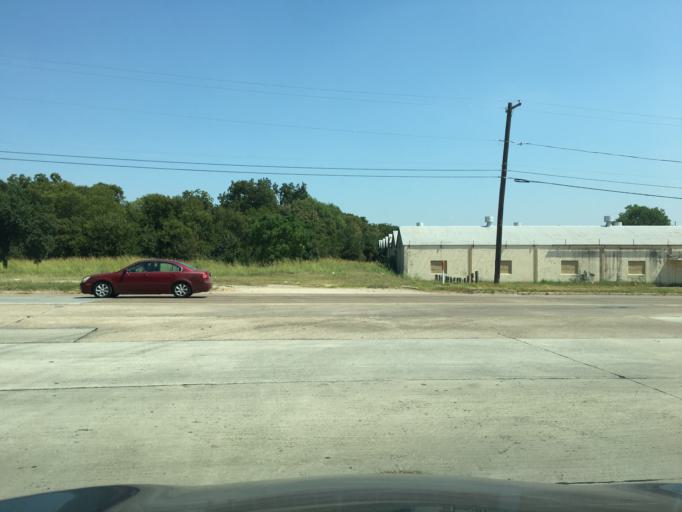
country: US
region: Texas
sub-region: Dallas County
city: Dallas
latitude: 32.7381
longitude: -96.7881
